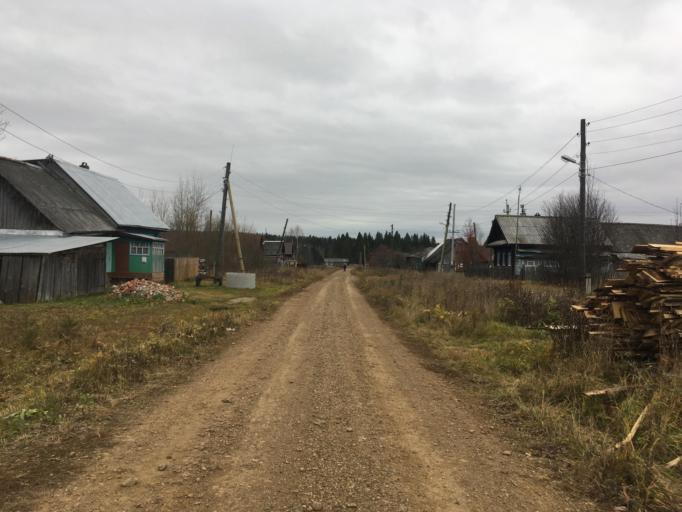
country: RU
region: Perm
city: Komarikhinskiy
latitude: 58.0904
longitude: 57.1107
